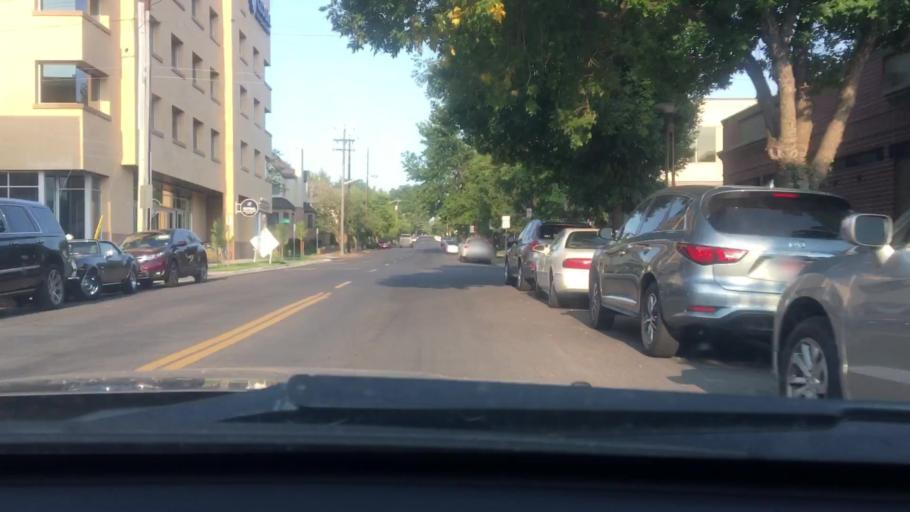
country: US
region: Colorado
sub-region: Arapahoe County
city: Glendale
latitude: 39.7194
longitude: -104.9496
